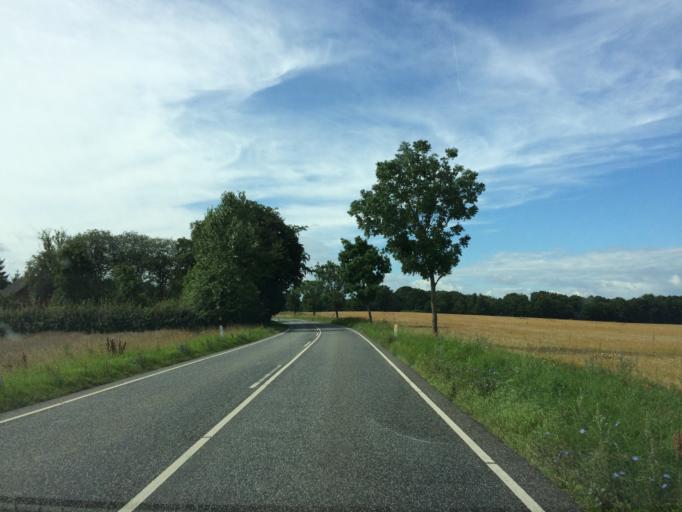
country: DK
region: South Denmark
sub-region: Odense Kommune
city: Bellinge
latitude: 55.2976
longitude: 10.2893
